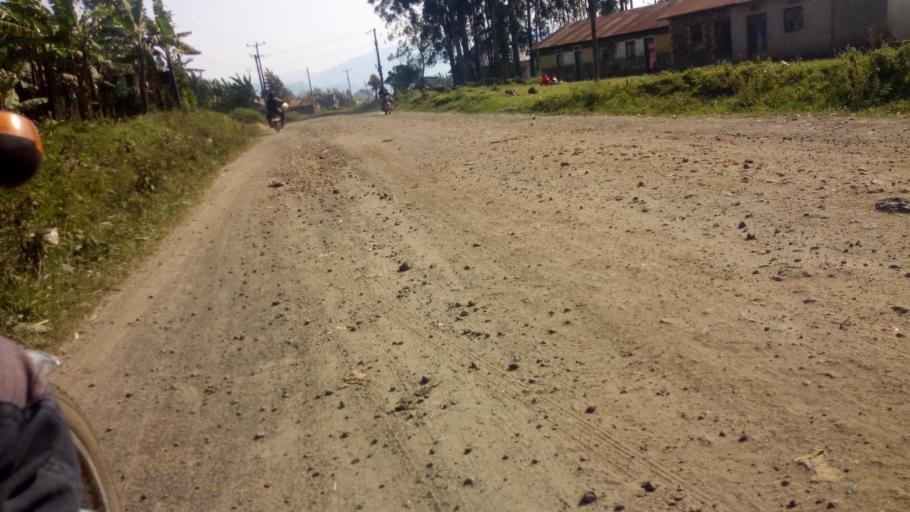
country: UG
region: Western Region
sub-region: Kisoro District
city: Kisoro
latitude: -1.2490
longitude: 29.7131
